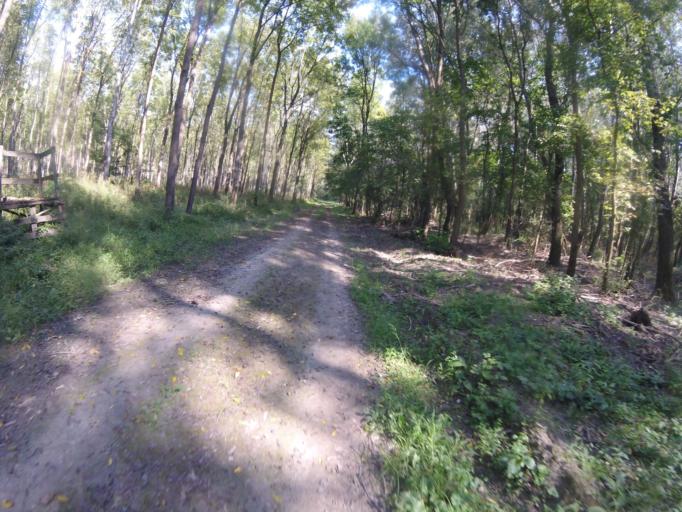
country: HU
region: Bacs-Kiskun
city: Baja
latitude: 46.2011
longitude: 18.8635
